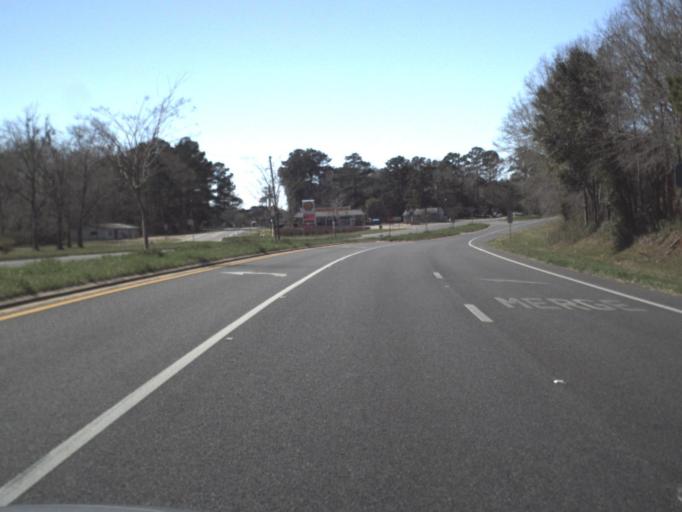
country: US
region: Florida
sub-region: Gadsden County
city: Gretna
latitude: 30.5910
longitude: -84.6404
